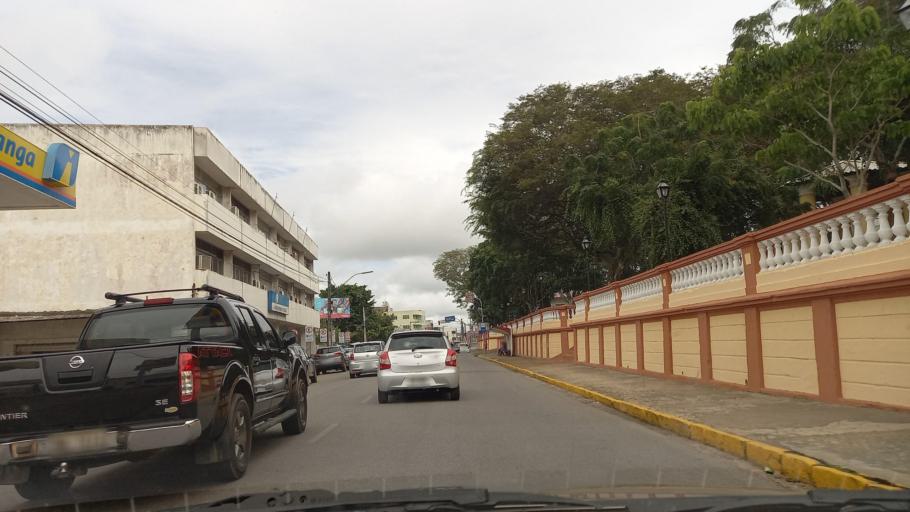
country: BR
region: Pernambuco
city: Garanhuns
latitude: -8.8888
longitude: -36.4924
